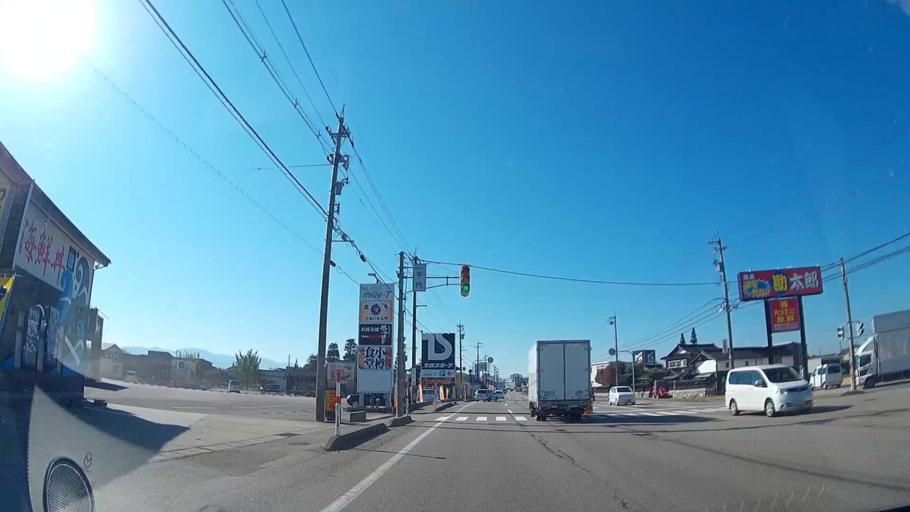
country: JP
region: Toyama
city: Takaoka
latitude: 36.6594
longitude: 136.9708
